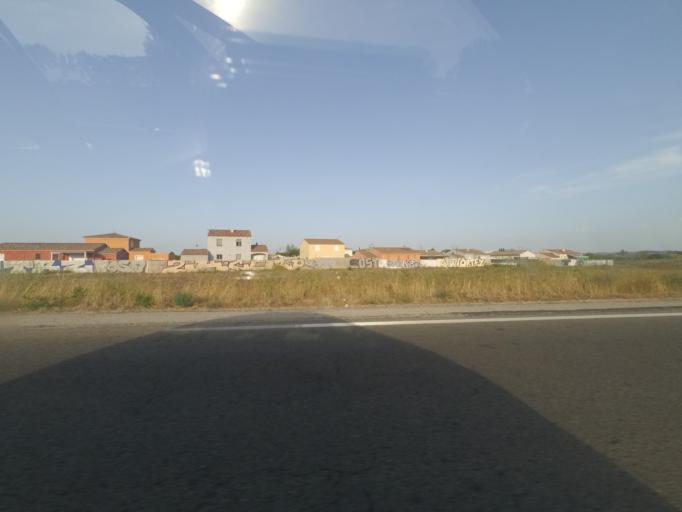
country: FR
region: Languedoc-Roussillon
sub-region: Departement du Gard
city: Bernis
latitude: 43.7653
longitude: 4.2788
